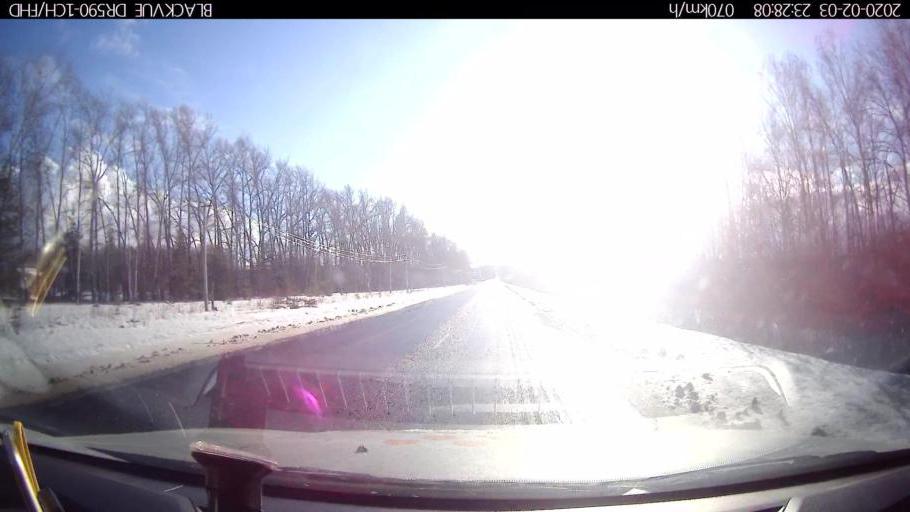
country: RU
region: Nizjnij Novgorod
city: Kstovo
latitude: 55.9746
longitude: 44.2107
